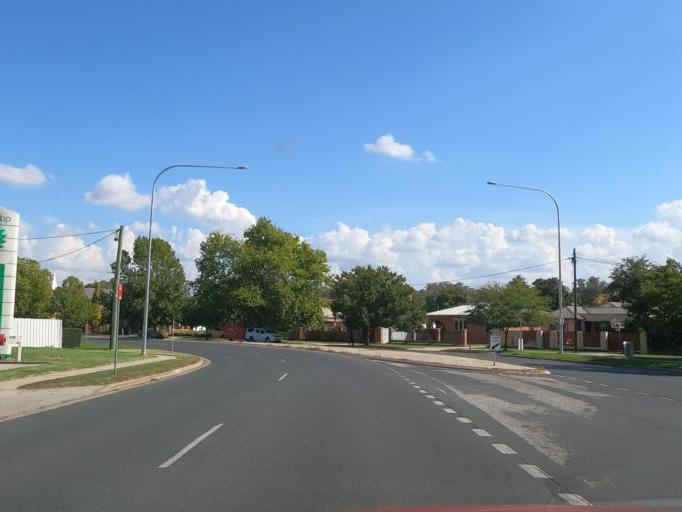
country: AU
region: New South Wales
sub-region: Albury Municipality
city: North Albury
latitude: -36.0638
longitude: 146.9251
